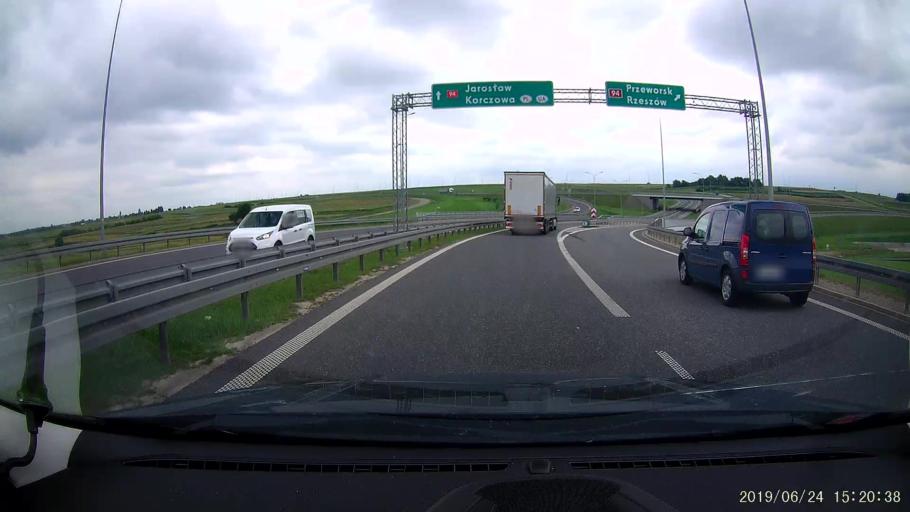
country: PL
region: Subcarpathian Voivodeship
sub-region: Powiat przeworski
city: Mirocin
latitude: 50.0398
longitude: 22.5769
